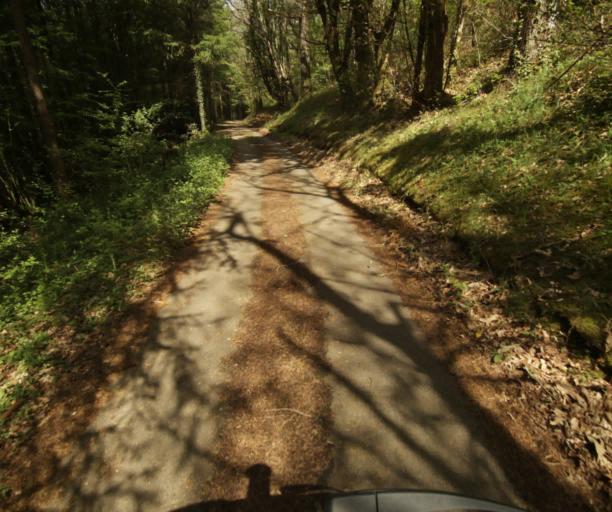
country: FR
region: Limousin
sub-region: Departement de la Correze
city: Naves
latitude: 45.2909
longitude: 1.7763
